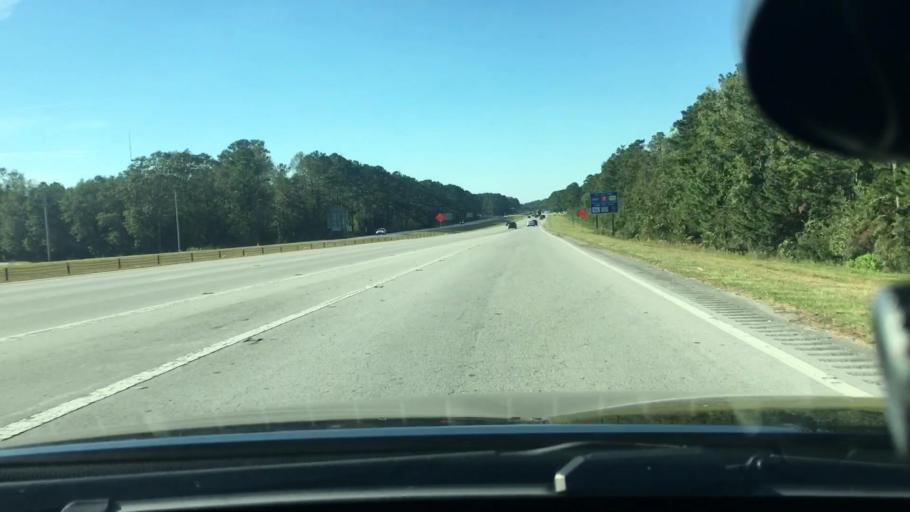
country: US
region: North Carolina
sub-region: Craven County
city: Trent Woods
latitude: 35.1059
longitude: -77.0868
